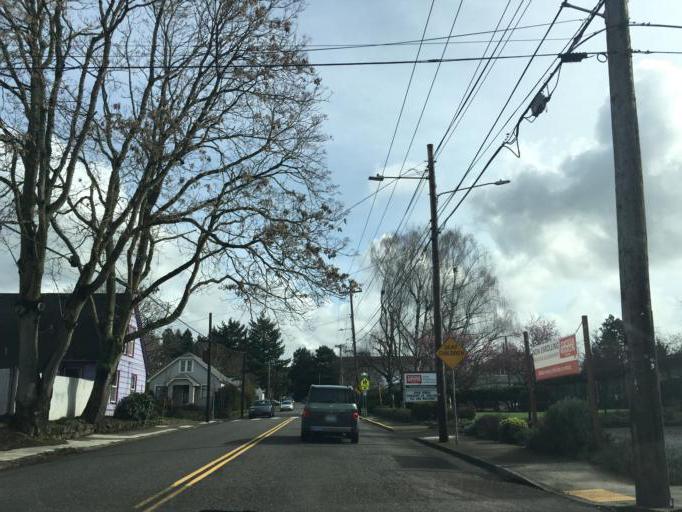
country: US
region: Oregon
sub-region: Clackamas County
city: Milwaukie
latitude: 45.4903
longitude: -122.6364
